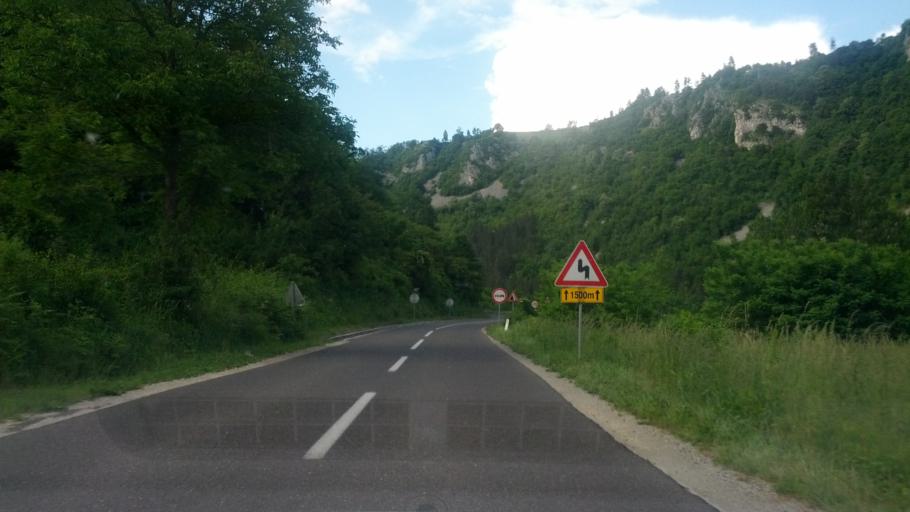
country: BA
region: Federation of Bosnia and Herzegovina
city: Stijena
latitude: 44.9064
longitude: 15.9903
